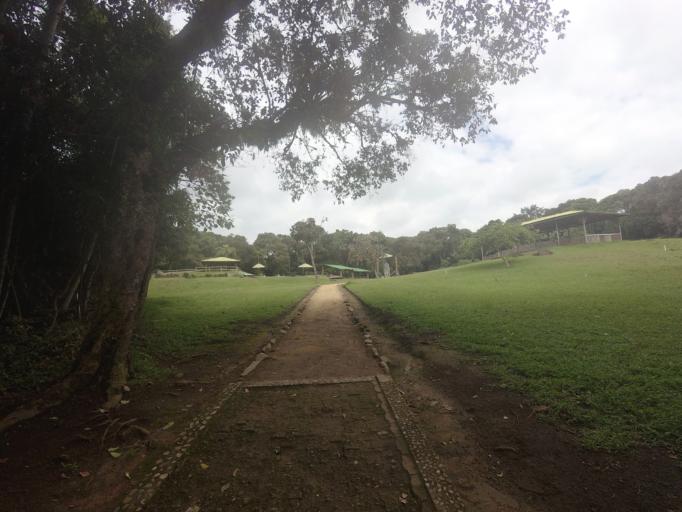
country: CO
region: Huila
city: San Agustin
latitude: 1.8835
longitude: -76.2964
